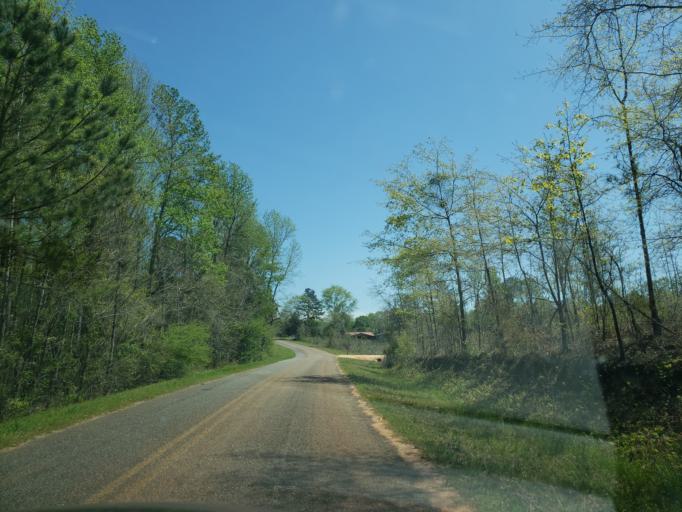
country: US
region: Alabama
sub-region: Tallapoosa County
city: Dadeville
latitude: 32.6705
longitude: -85.7505
